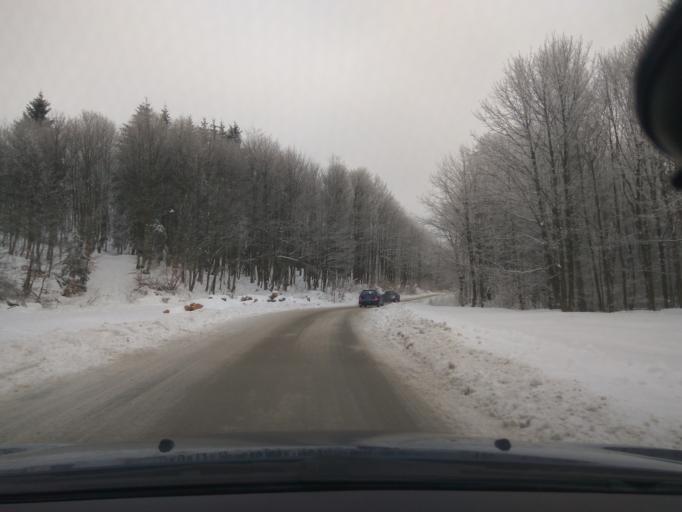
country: CZ
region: Zlin
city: Strani
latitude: 48.8526
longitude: 17.6774
